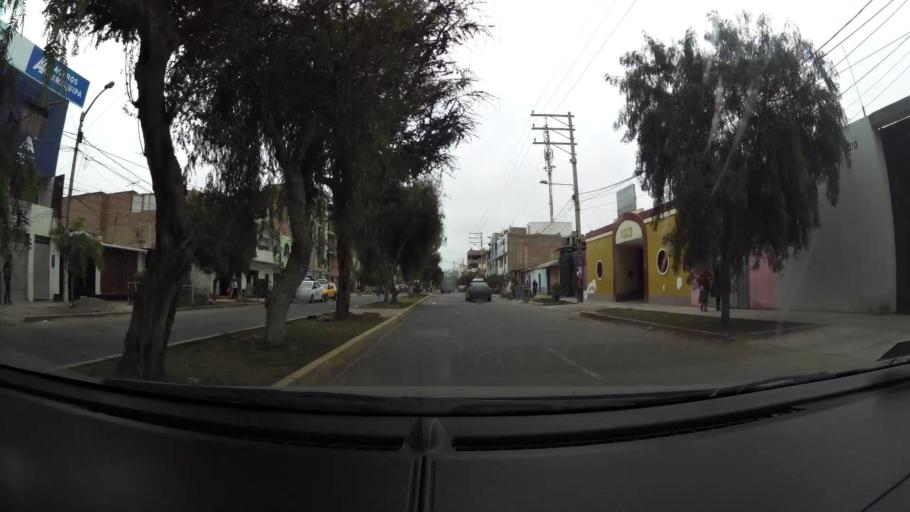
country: PE
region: La Libertad
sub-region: Provincia de Trujillo
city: Buenos Aires
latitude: -8.1380
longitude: -79.0446
